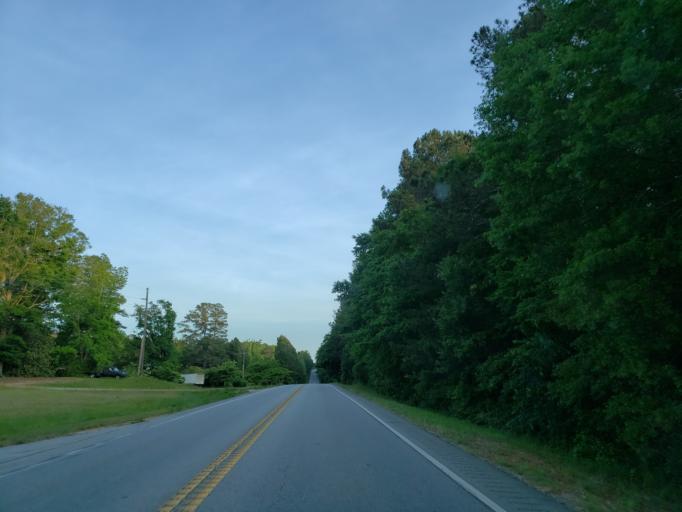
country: US
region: Georgia
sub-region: Coweta County
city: Newnan
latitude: 33.4549
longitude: -84.8864
